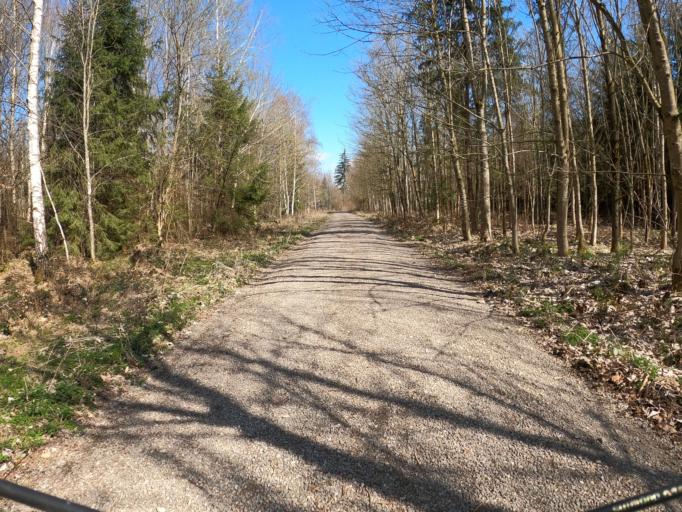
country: DE
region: Bavaria
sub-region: Swabia
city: Nersingen
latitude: 48.4038
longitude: 10.1586
